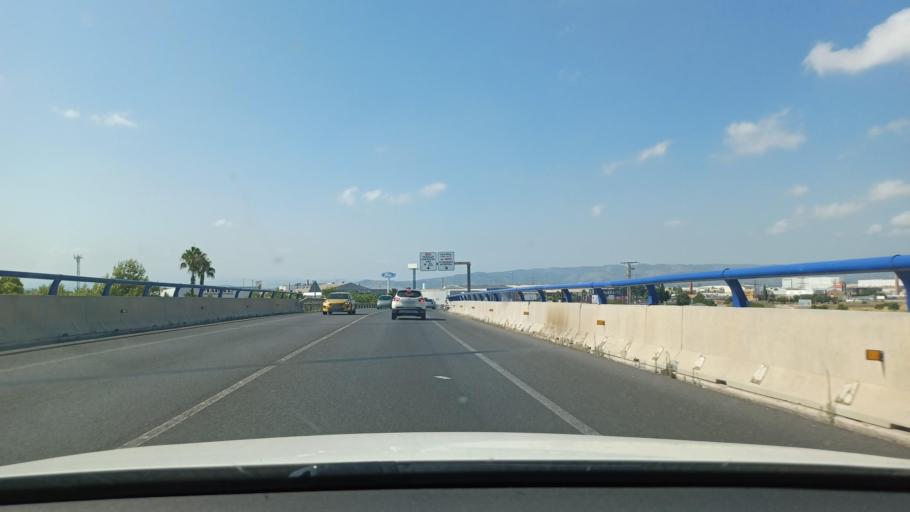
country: ES
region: Valencia
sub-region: Provincia de Castello
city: Vila-real
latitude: 39.9436
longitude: -0.0869
